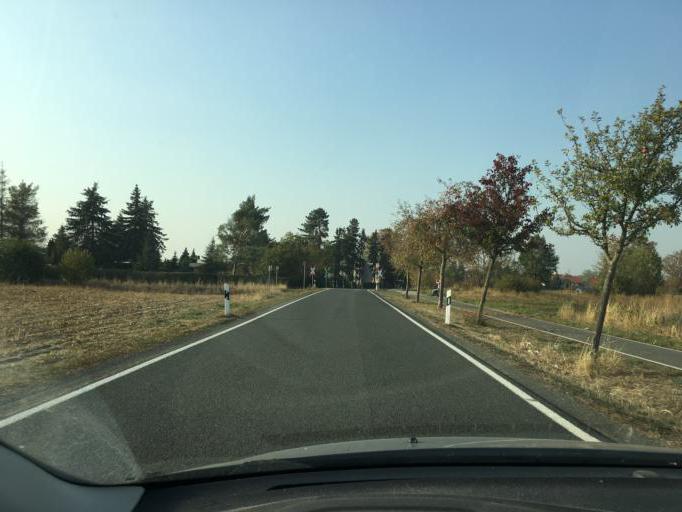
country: DE
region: Saxony
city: Wurzen
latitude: 51.3567
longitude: 12.7466
